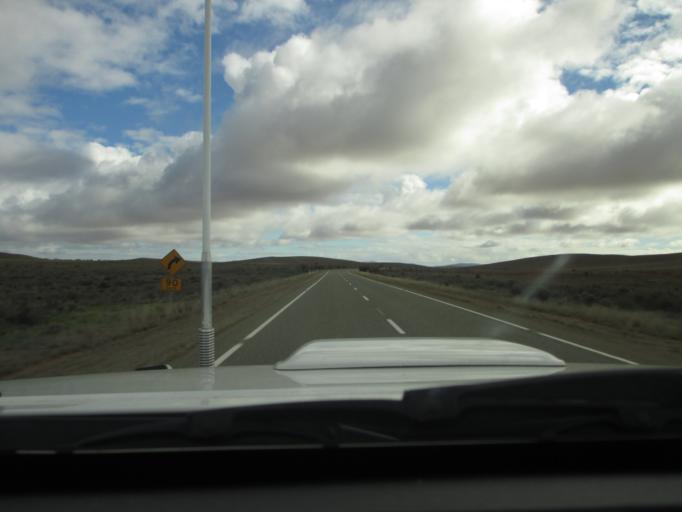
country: AU
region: South Australia
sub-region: Flinders Ranges
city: Quorn
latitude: -32.1515
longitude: 138.5237
